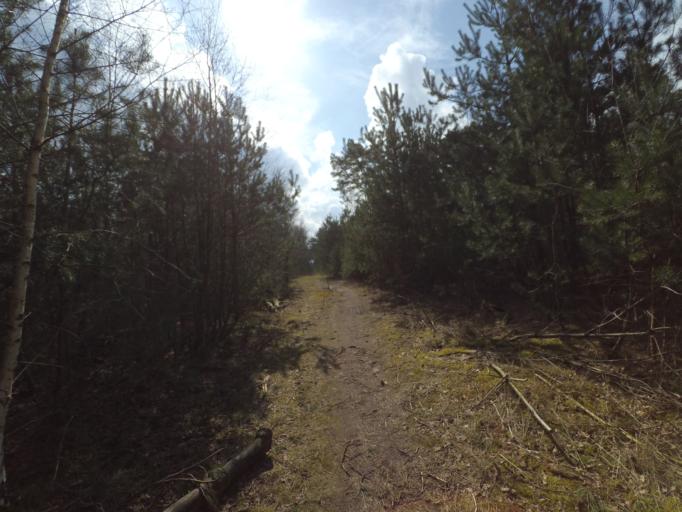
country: NL
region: Utrecht
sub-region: Gemeente Amersfoort
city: Amersfoort
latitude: 52.1211
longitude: 5.3741
